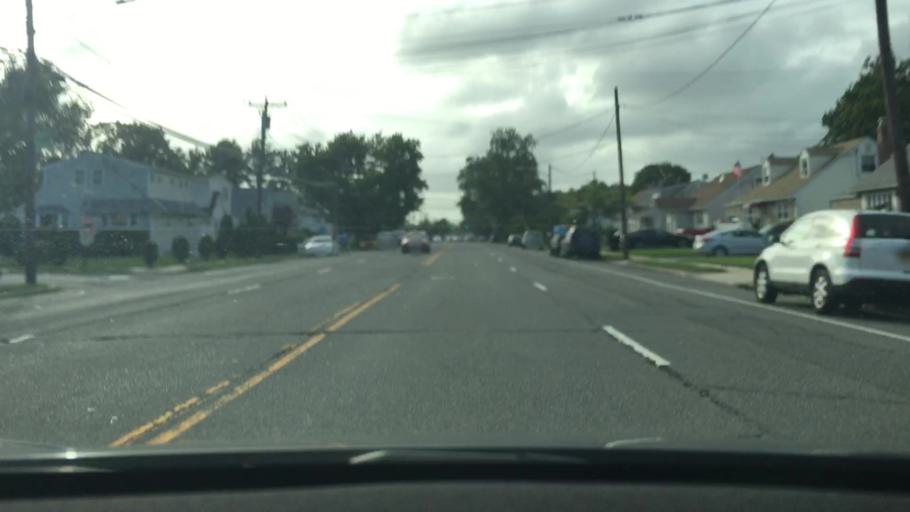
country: US
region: New York
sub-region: Nassau County
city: Hicksville
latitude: 40.7756
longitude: -73.5232
